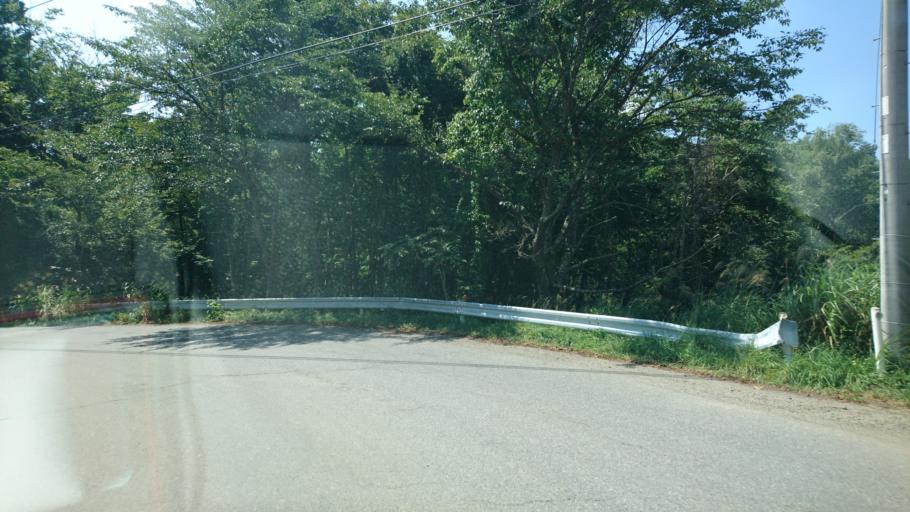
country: JP
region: Gunma
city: Numata
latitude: 36.7654
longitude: 139.2512
